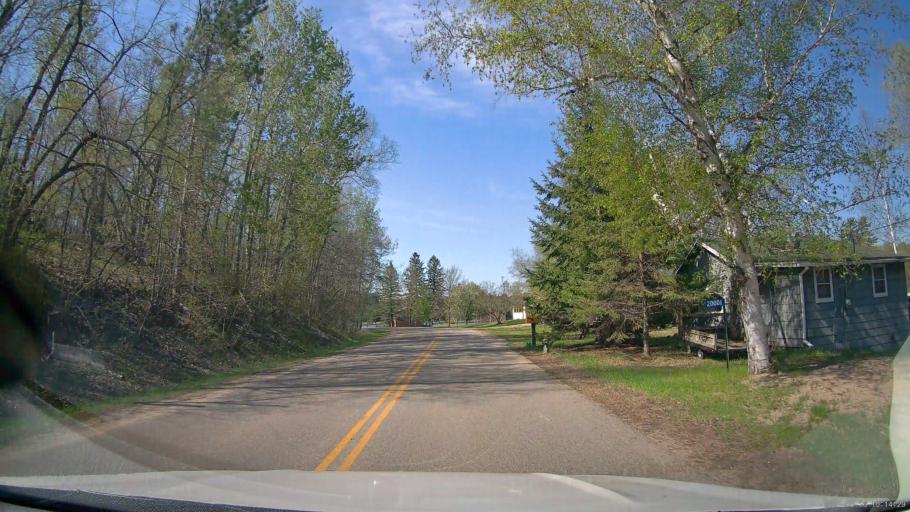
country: US
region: Minnesota
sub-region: Hubbard County
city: Park Rapids
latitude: 46.9816
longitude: -94.9515
